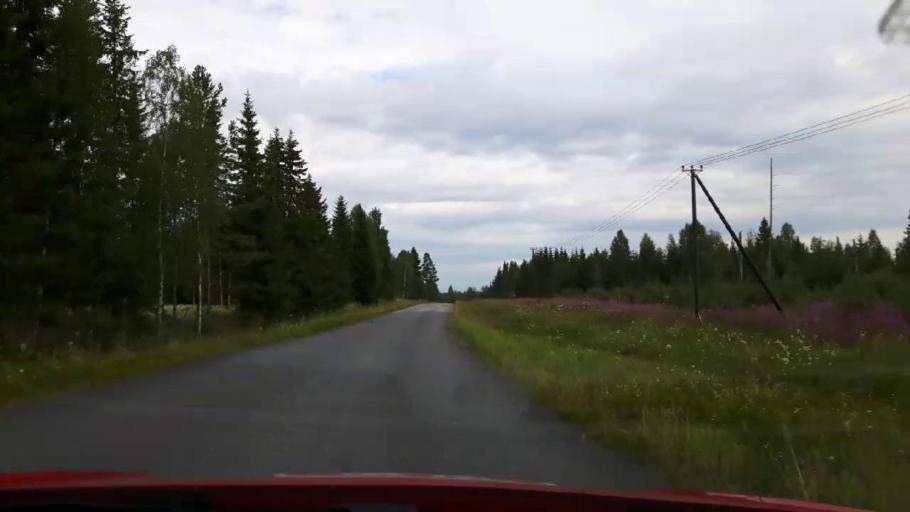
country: SE
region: Jaemtland
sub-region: Stroemsunds Kommun
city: Stroemsund
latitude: 63.5327
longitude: 15.3542
